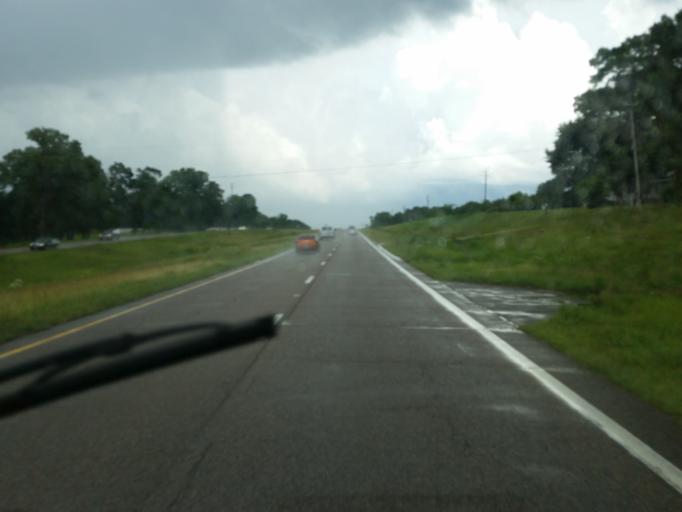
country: US
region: Mississippi
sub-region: George County
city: Lucedale
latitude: 30.9075
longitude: -88.4762
